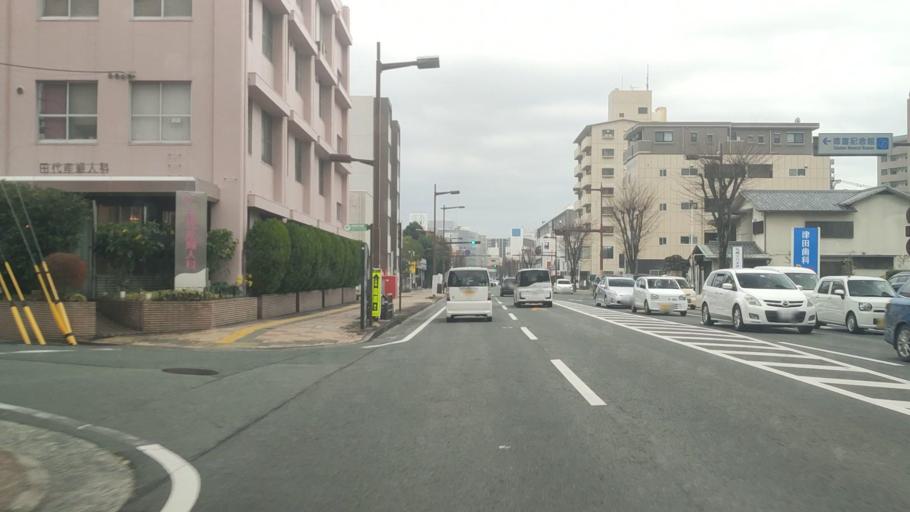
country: JP
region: Kumamoto
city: Kumamoto
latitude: 32.8034
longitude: 130.7204
